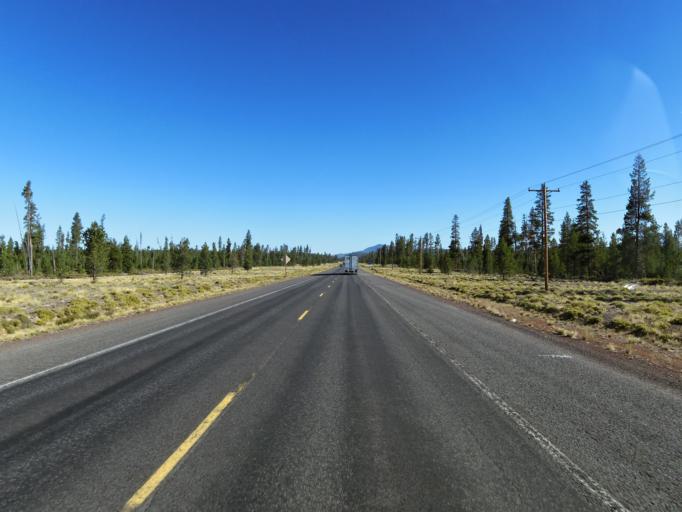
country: US
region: Oregon
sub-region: Deschutes County
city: La Pine
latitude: 43.1550
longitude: -121.7943
